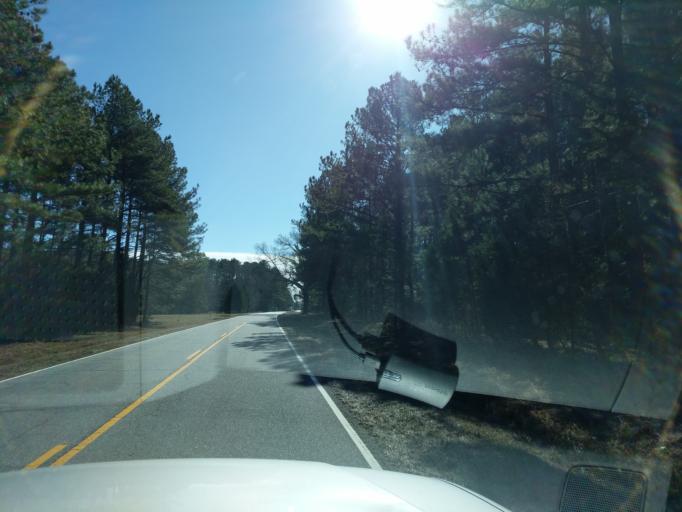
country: US
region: South Carolina
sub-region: Saluda County
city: Saluda
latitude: 34.0855
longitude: -81.8246
